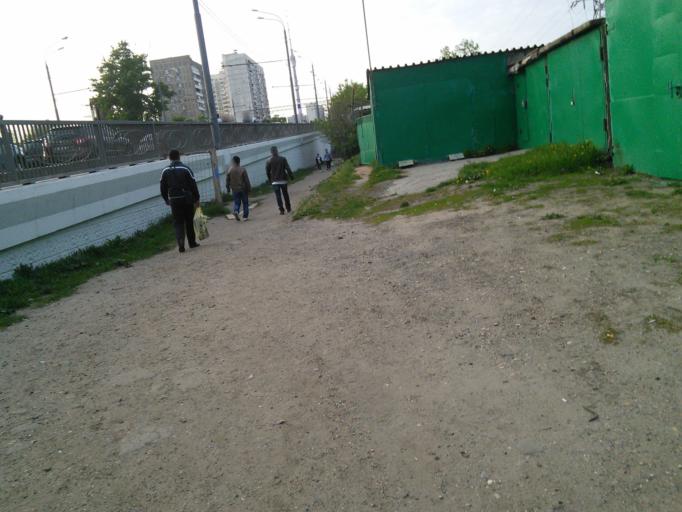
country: RU
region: Moscow
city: Mar'ina Roshcha
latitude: 55.7994
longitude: 37.6161
